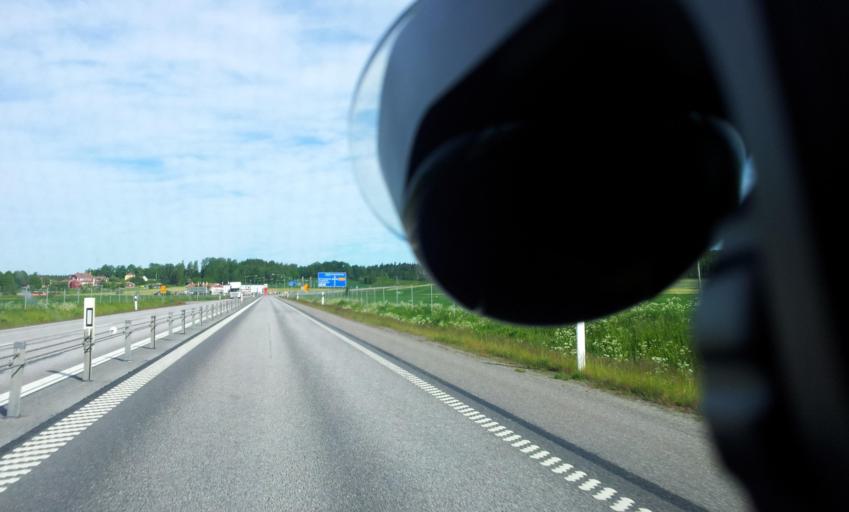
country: SE
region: OEstergoetland
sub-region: Valdemarsviks Kommun
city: Gusum
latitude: 58.3315
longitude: 16.4641
